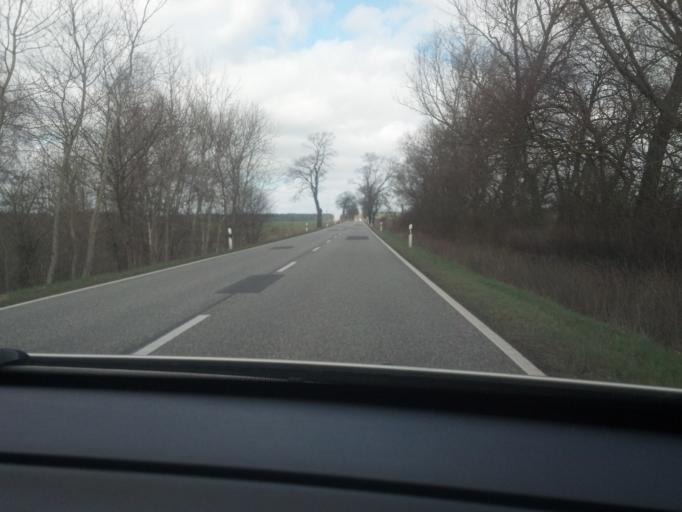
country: DE
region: Brandenburg
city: Gerdshagen
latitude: 53.3422
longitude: 12.2465
